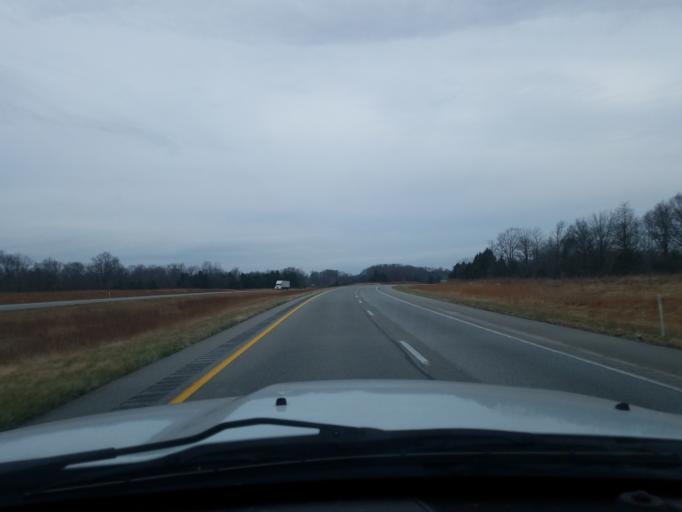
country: US
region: Indiana
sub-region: Harrison County
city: Corydon
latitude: 38.2505
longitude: -86.2720
